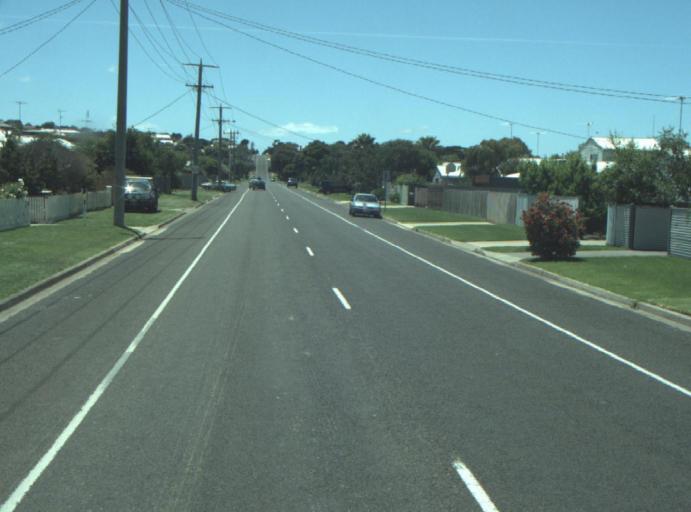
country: AU
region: Victoria
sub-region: Greater Geelong
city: Clifton Springs
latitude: -38.2665
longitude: 144.5518
